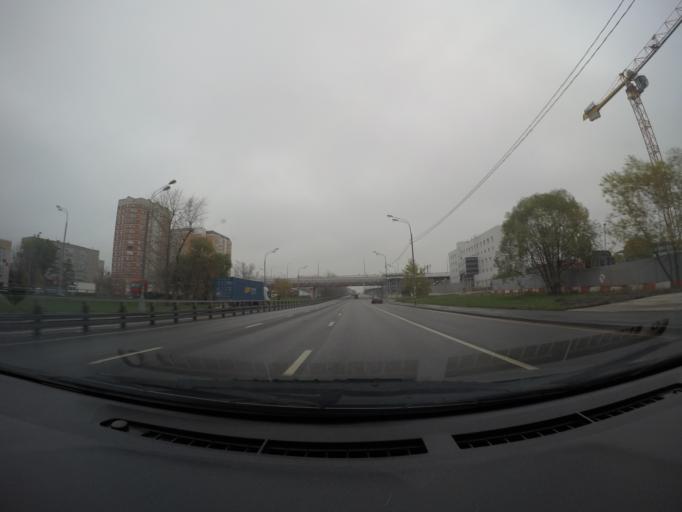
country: RU
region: Moskovskaya
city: Shcherbinka
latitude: 55.5051
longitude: 37.5736
